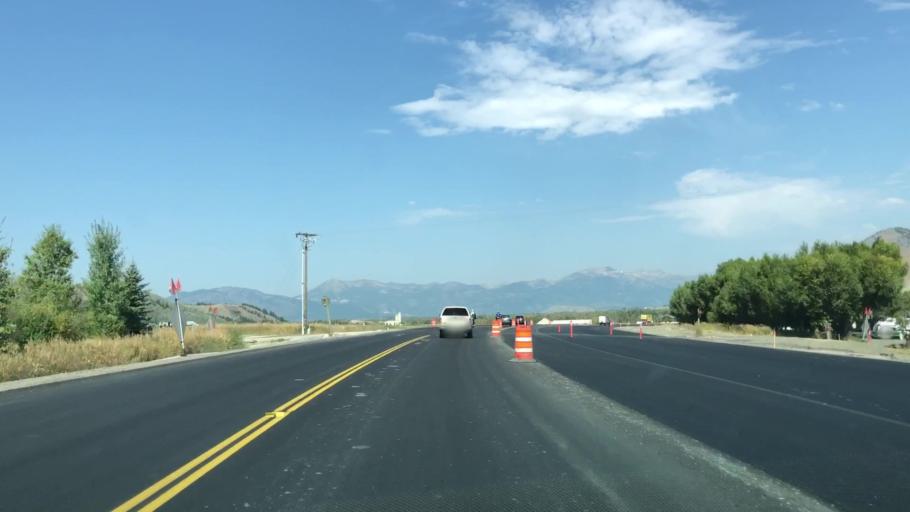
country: US
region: Wyoming
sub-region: Teton County
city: South Park
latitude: 43.3725
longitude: -110.7429
